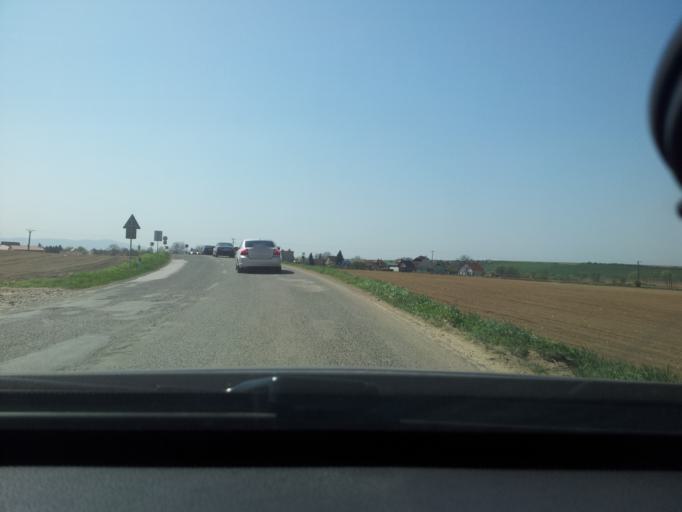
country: SK
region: Nitriansky
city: Banovce nad Bebravou
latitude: 48.6997
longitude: 18.2499
